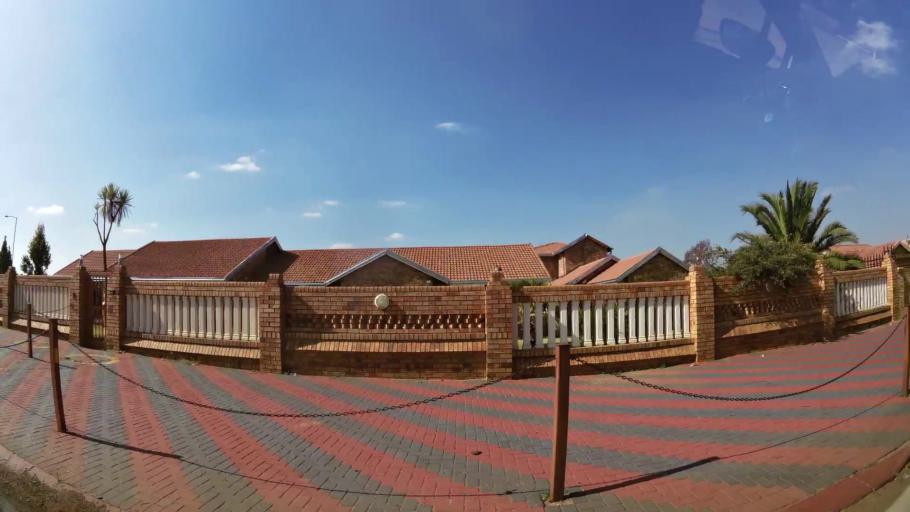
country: ZA
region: Gauteng
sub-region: City of Johannesburg Metropolitan Municipality
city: Roodepoort
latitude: -26.1659
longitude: 27.8016
